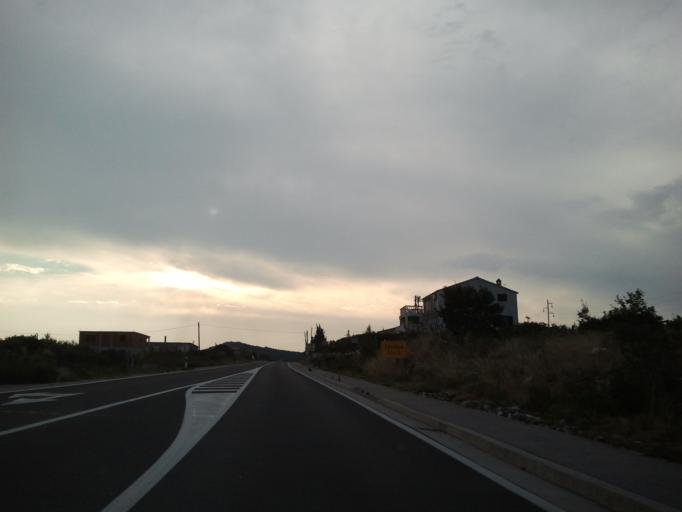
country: HR
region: Zadarska
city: Posedarje
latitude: 44.2202
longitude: 15.4536
